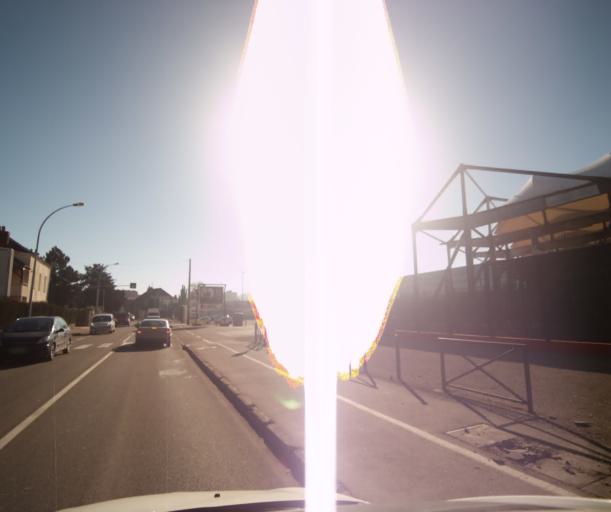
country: FR
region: Franche-Comte
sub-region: Departement du Doubs
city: Besancon
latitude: 47.2446
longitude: 6.0040
